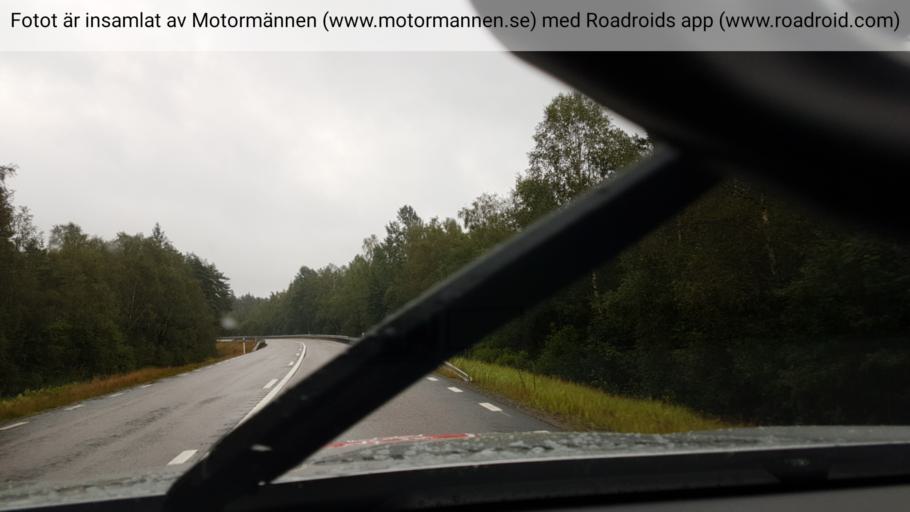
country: SE
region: Vaestra Goetaland
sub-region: Dals-Ed Kommun
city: Ed
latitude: 58.8731
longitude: 11.8414
